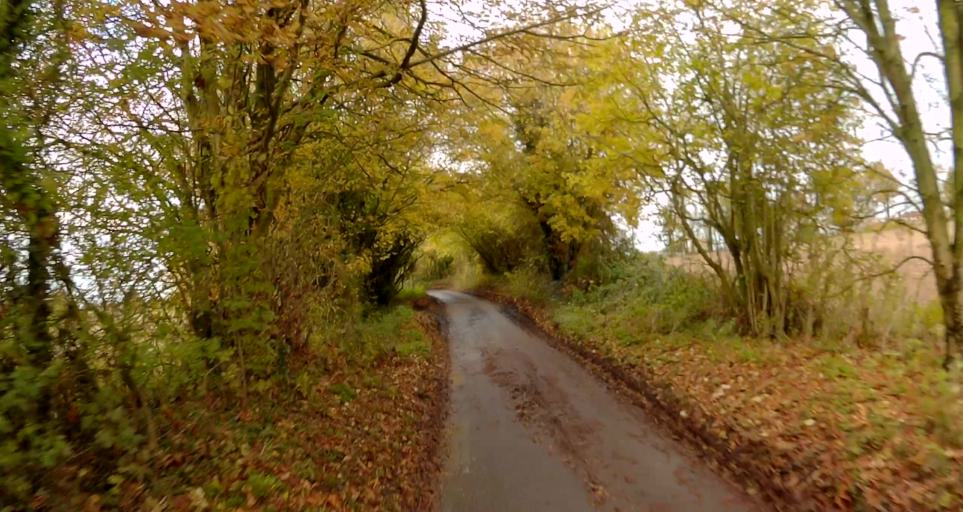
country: GB
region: England
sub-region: Hampshire
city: Long Sutton
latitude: 51.2145
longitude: -0.9431
